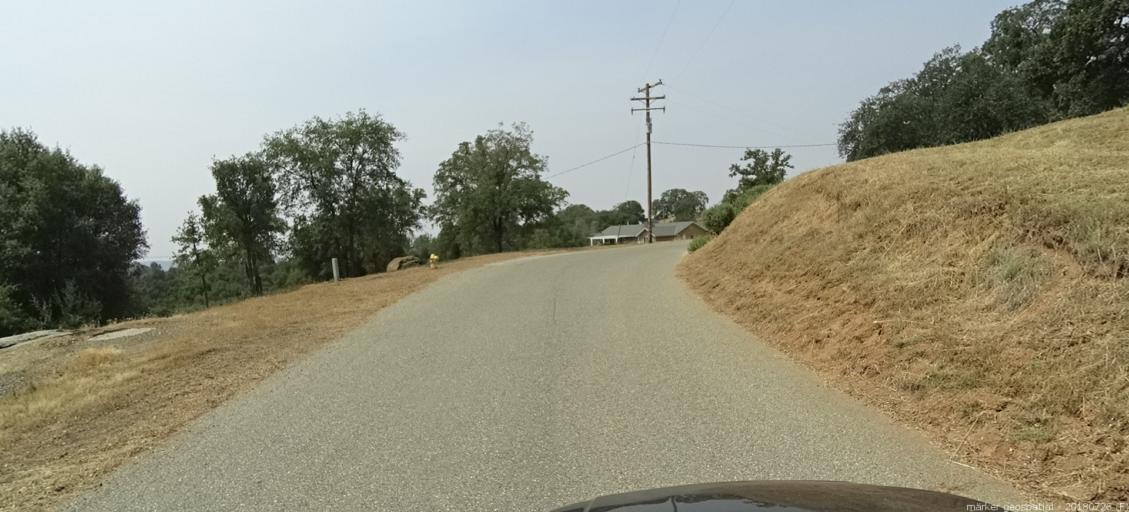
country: US
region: California
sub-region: Madera County
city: Coarsegold
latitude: 37.2529
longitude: -119.6894
